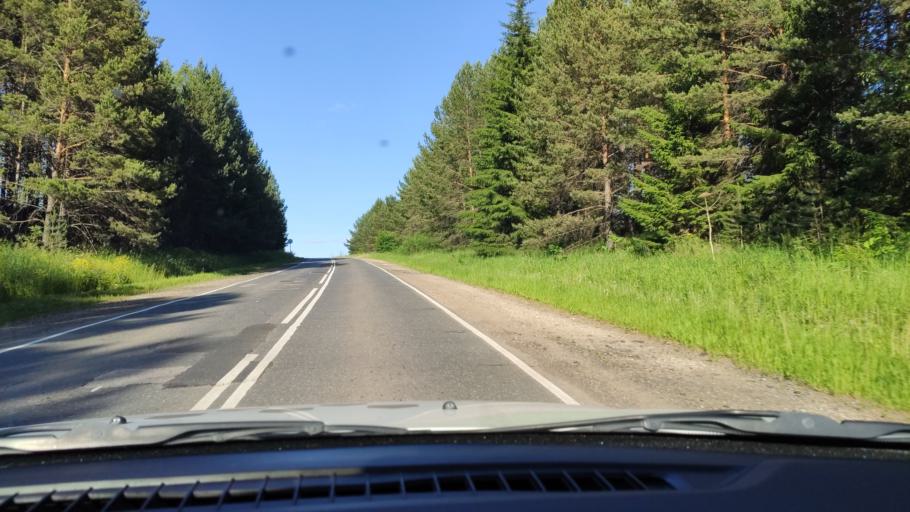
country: RU
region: Perm
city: Orda
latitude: 57.3377
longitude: 56.7712
